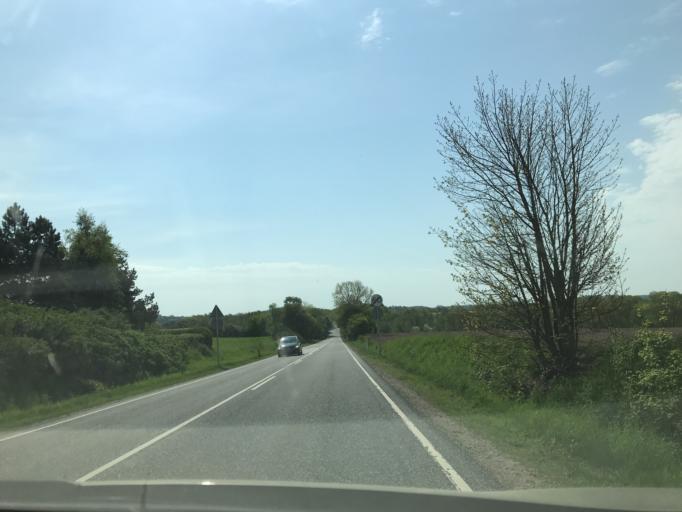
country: DK
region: South Denmark
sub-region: Middelfart Kommune
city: Ejby
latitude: 55.3752
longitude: 9.9187
